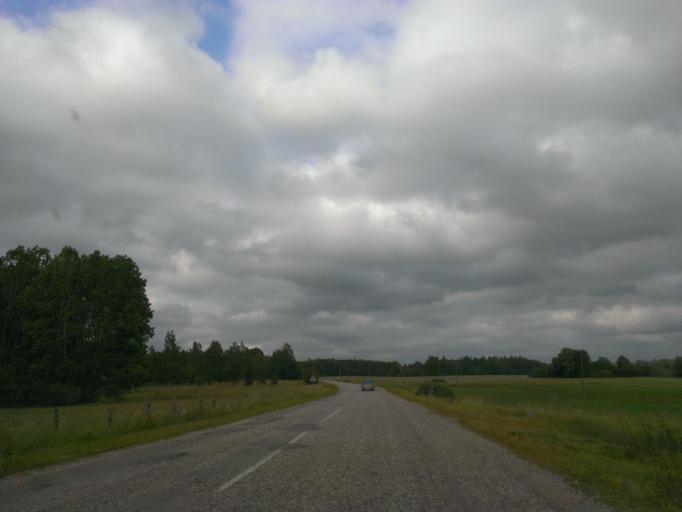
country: LV
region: Skrunda
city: Skrunda
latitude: 56.6955
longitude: 21.8212
